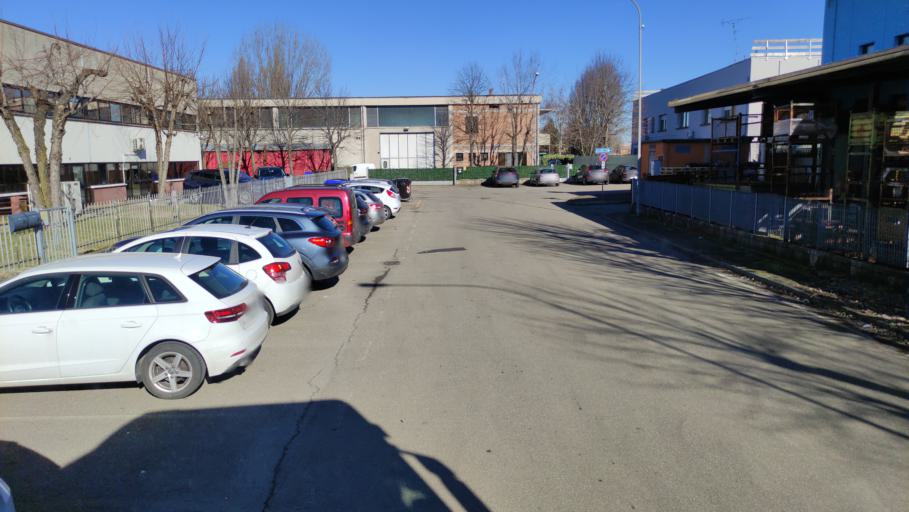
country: IT
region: Emilia-Romagna
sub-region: Provincia di Reggio Emilia
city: San Martino in Rio
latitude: 44.7332
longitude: 10.7742
